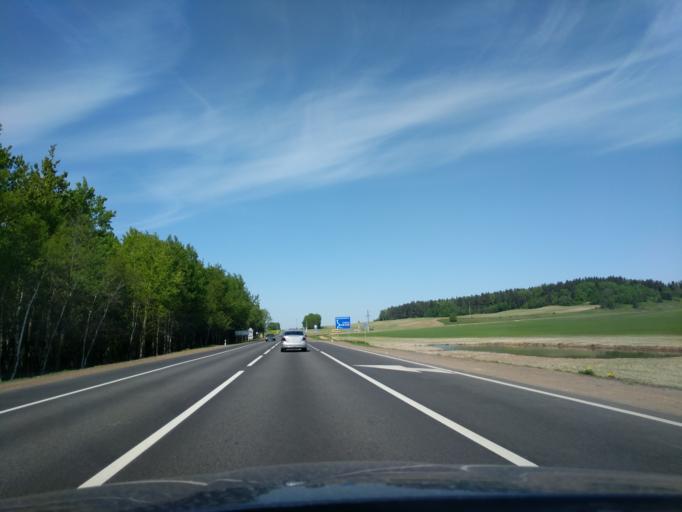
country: BY
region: Minsk
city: Bal'shavik
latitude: 54.0883
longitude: 27.5407
